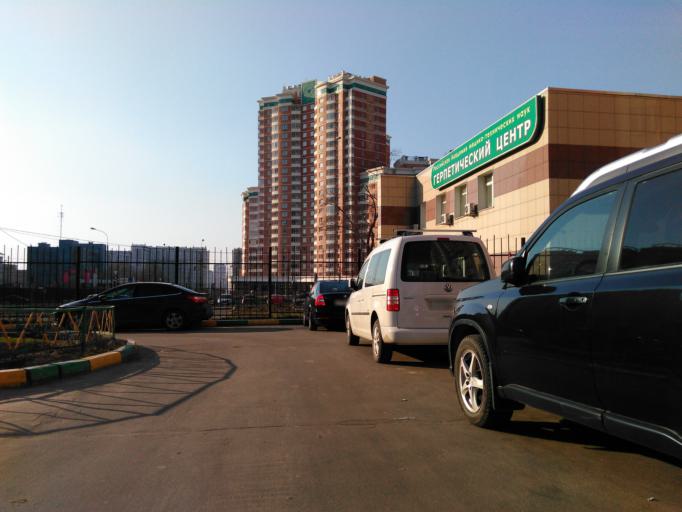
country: RU
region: Moscow
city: Ramenki
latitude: 55.6983
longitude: 37.5029
